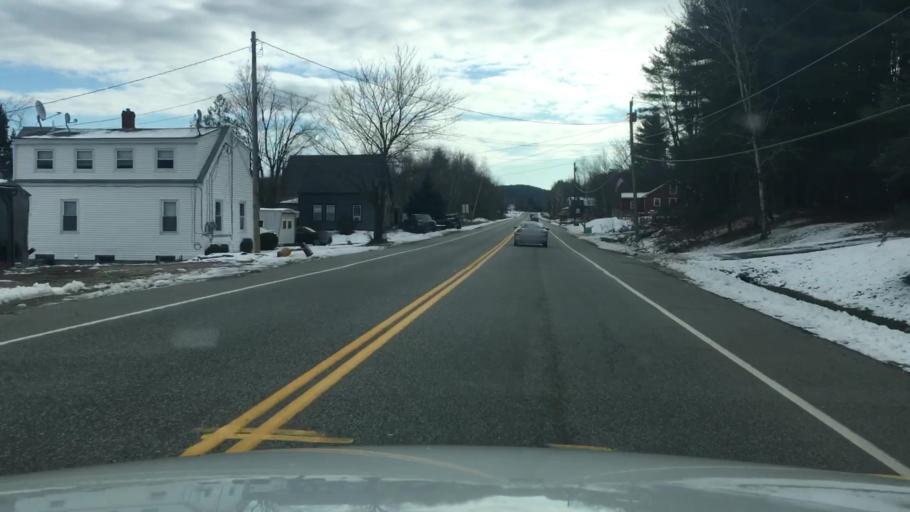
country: US
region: Maine
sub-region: Oxford County
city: Canton
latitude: 44.4389
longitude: -70.3129
